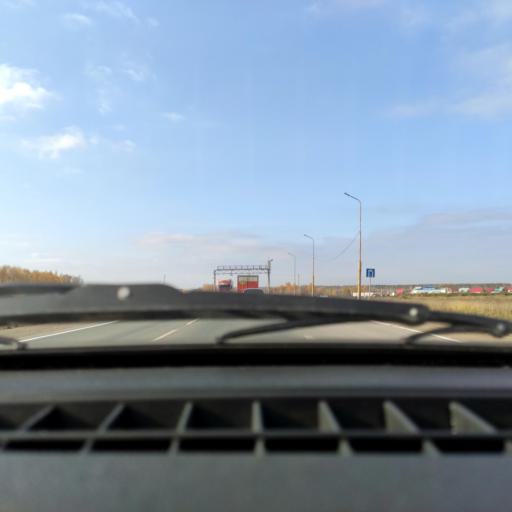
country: RU
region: Bashkortostan
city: Iglino
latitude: 54.7378
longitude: 56.2867
